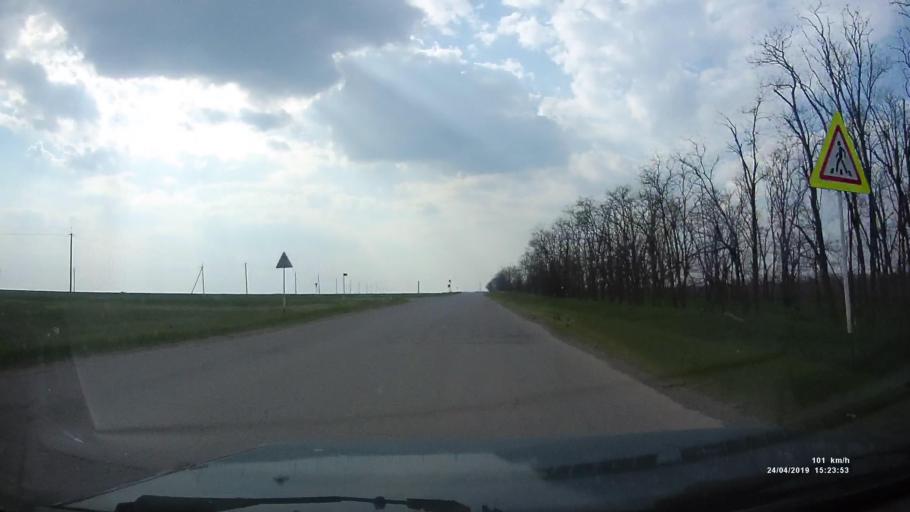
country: RU
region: Rostov
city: Remontnoye
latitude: 46.5453
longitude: 43.0806
